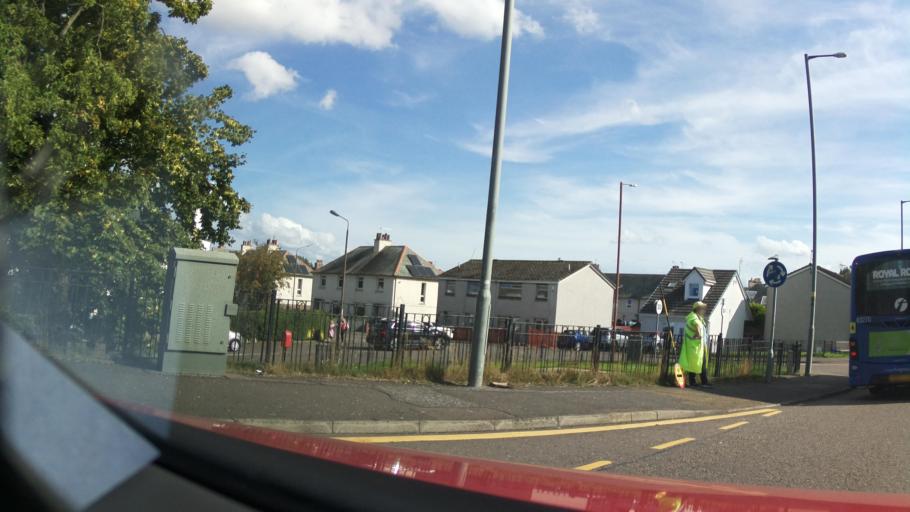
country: GB
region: Scotland
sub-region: Stirling
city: Bannockburn
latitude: 56.0943
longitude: -3.9208
